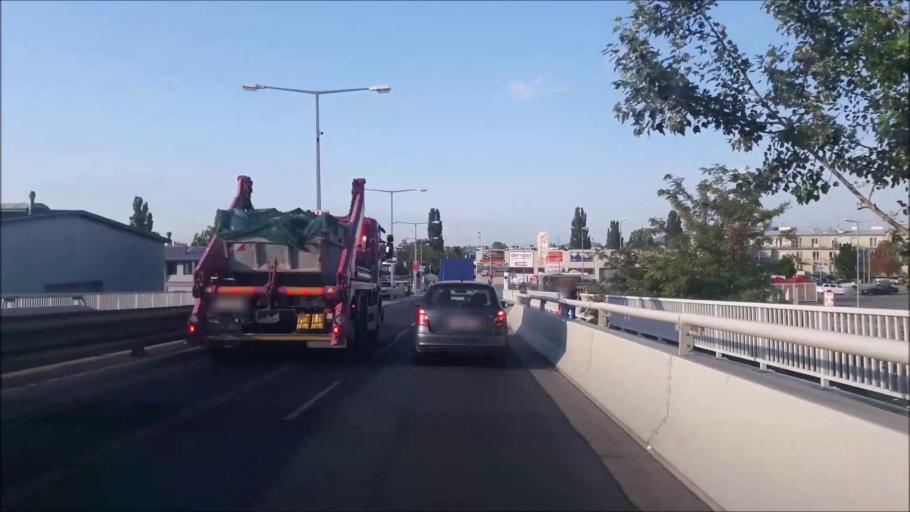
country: AT
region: Lower Austria
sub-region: Politischer Bezirk Modling
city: Vosendorf
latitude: 48.1494
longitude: 16.3618
